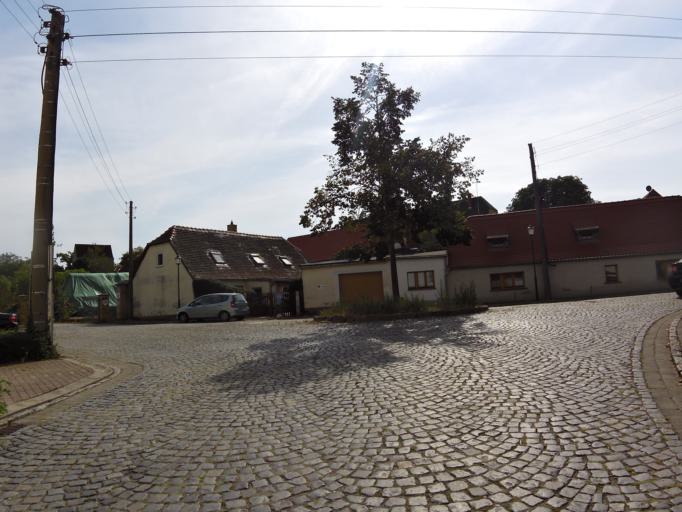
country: DE
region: Saxony
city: Schkeuditz
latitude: 51.3632
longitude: 12.2708
